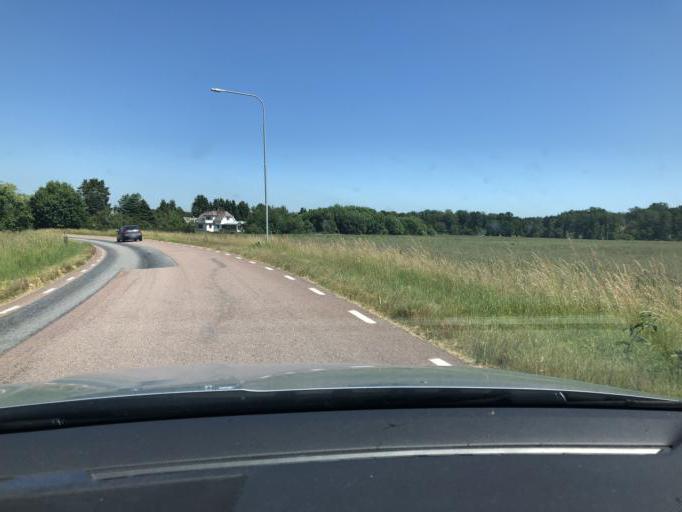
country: SE
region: Blekinge
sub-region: Olofstroms Kommun
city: Jamshog
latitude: 56.1785
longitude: 14.6119
